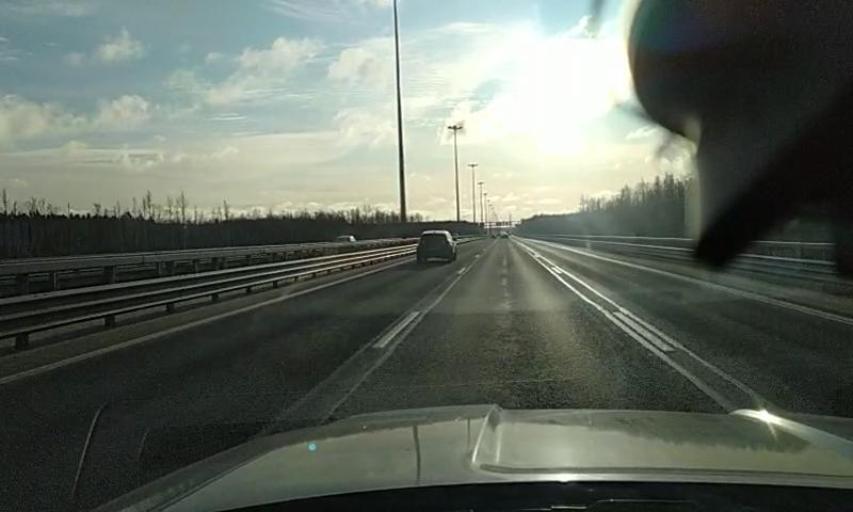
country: RU
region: St.-Petersburg
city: Pesochnyy
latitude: 60.1061
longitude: 30.0860
